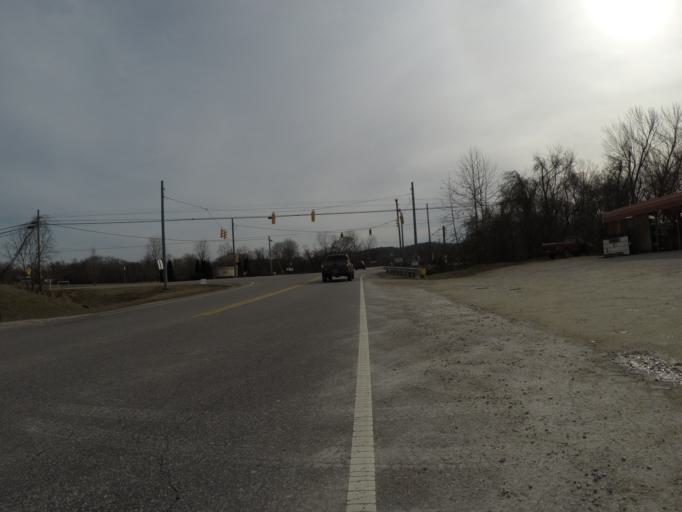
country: US
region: West Virginia
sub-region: Cabell County
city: Pea Ridge
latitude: 38.4433
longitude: -82.3770
